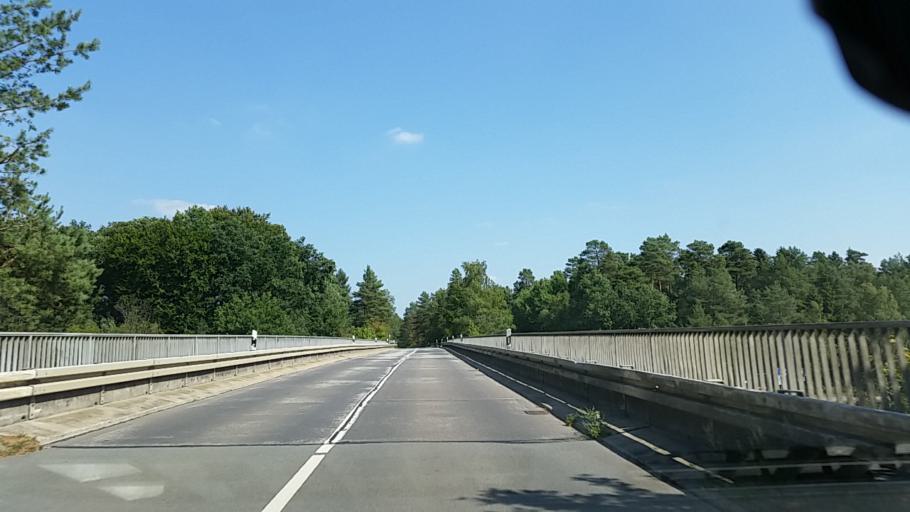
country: DE
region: Lower Saxony
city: Vastorf
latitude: 53.1715
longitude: 10.5177
